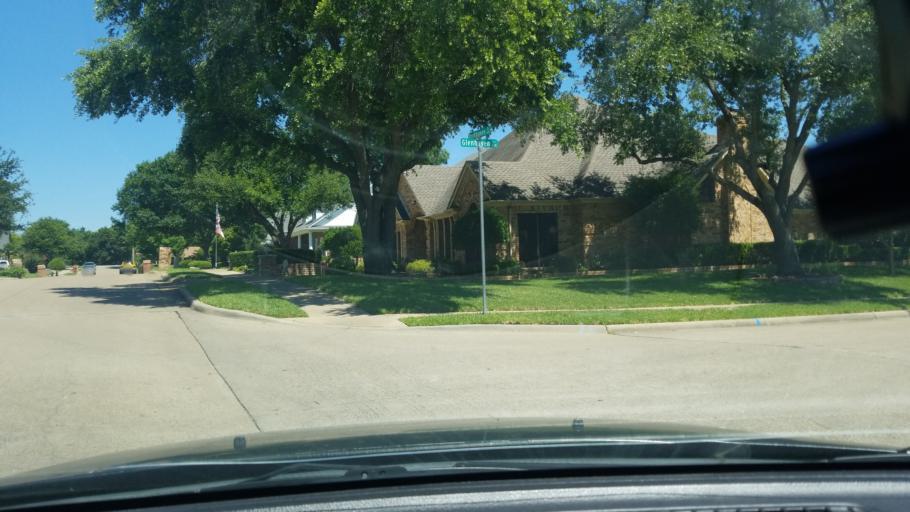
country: US
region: Texas
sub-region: Dallas County
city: Mesquite
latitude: 32.7598
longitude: -96.6069
